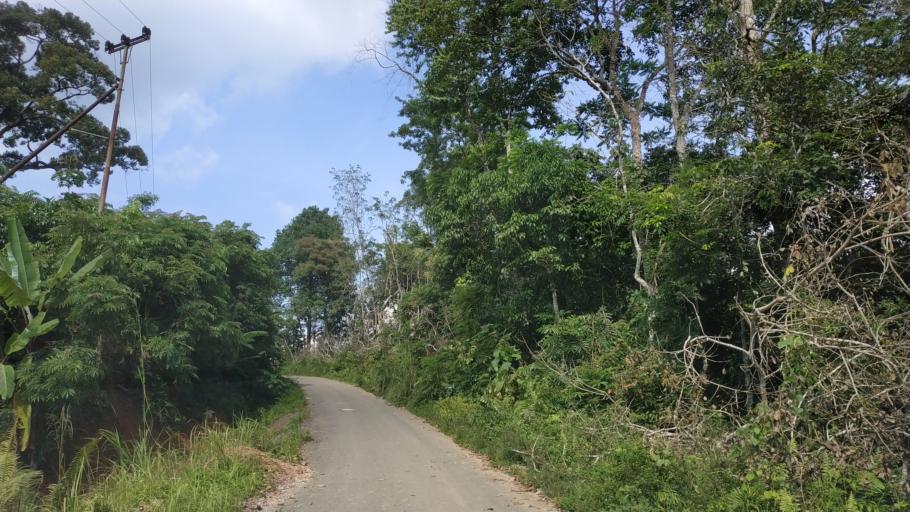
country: ID
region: Riau
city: Pangkalan Kasai
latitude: -0.7259
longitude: 102.4779
